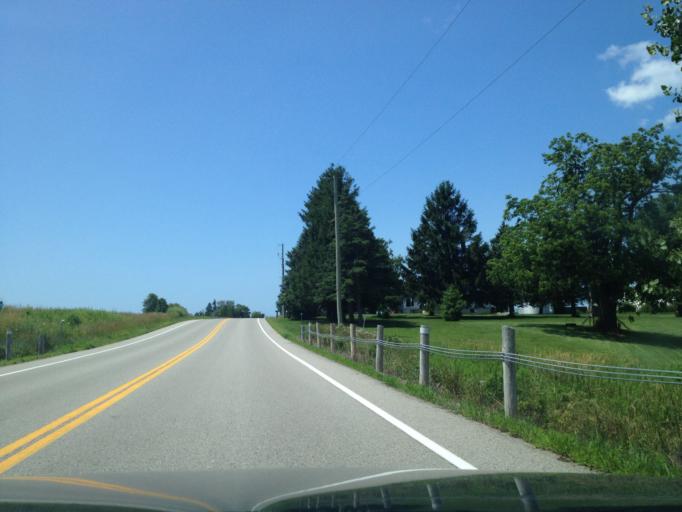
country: CA
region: Ontario
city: Norfolk County
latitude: 42.5780
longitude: -80.5330
